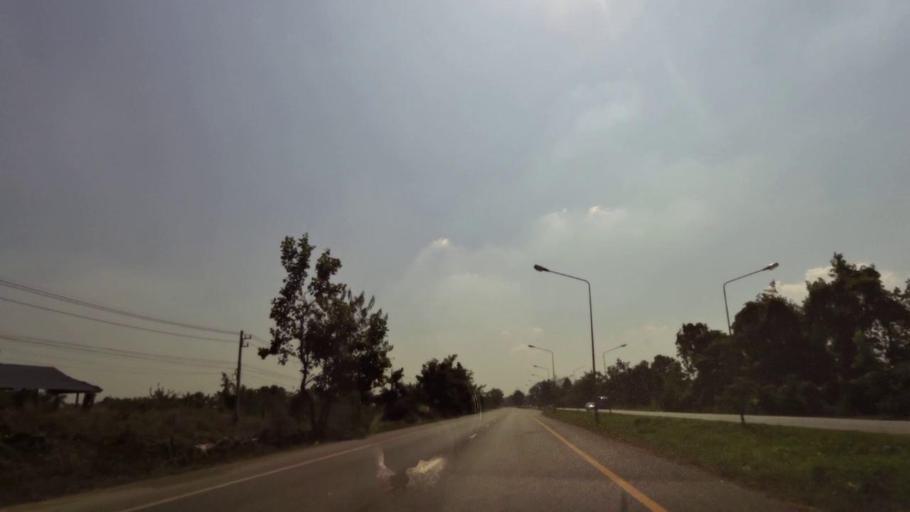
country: TH
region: Phichit
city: Bueng Na Rang
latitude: 16.2446
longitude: 100.1255
